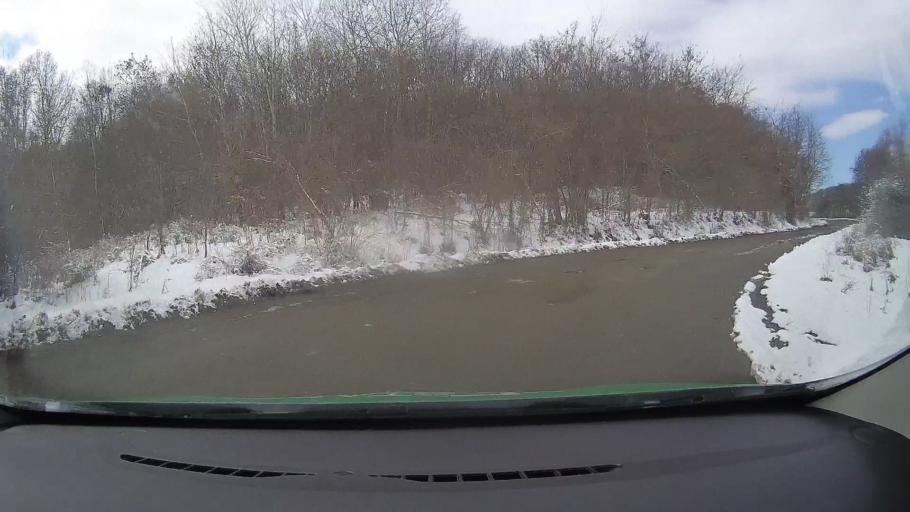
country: RO
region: Sibiu
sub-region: Comuna Altina
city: Altina
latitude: 45.9908
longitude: 24.4336
